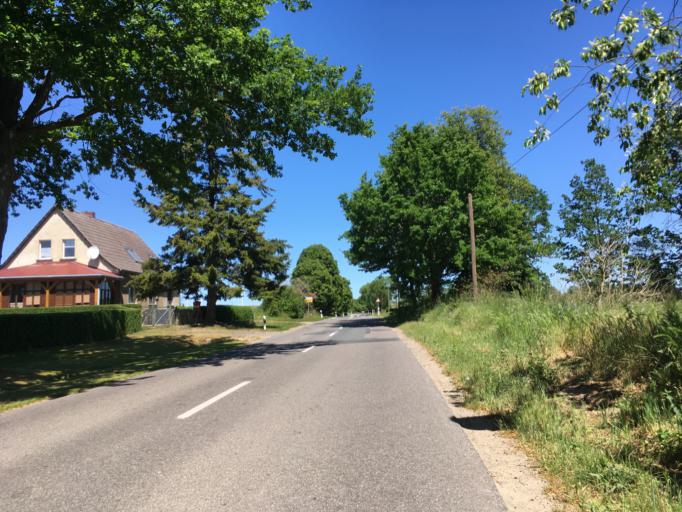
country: DE
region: Brandenburg
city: Zehdenick
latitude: 52.9356
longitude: 13.2660
